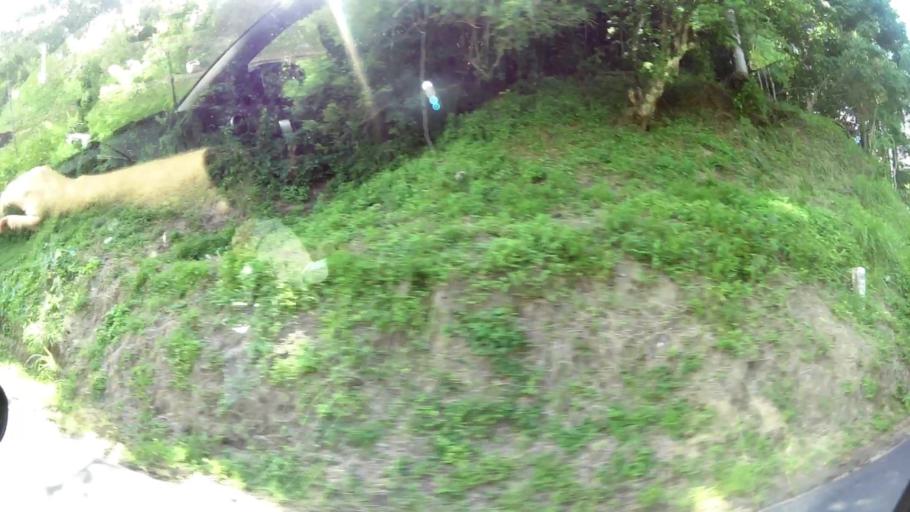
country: TT
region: Tobago
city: Scarborough
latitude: 11.2249
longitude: -60.7566
